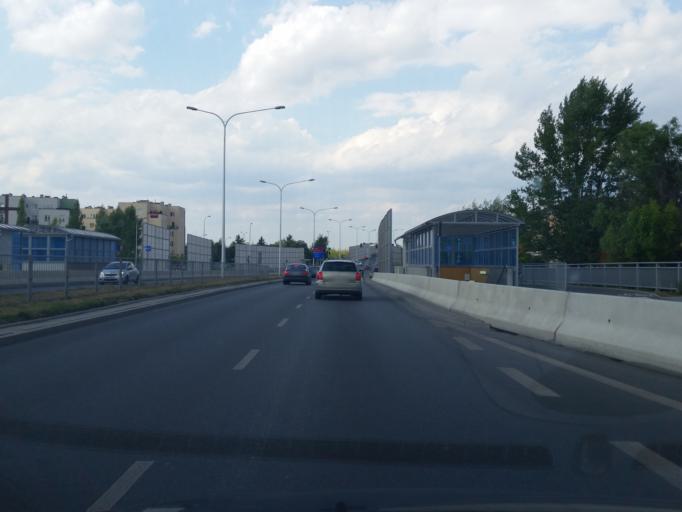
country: PL
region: Masovian Voivodeship
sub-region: Warszawa
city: Ursus
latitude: 52.1982
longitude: 20.9039
